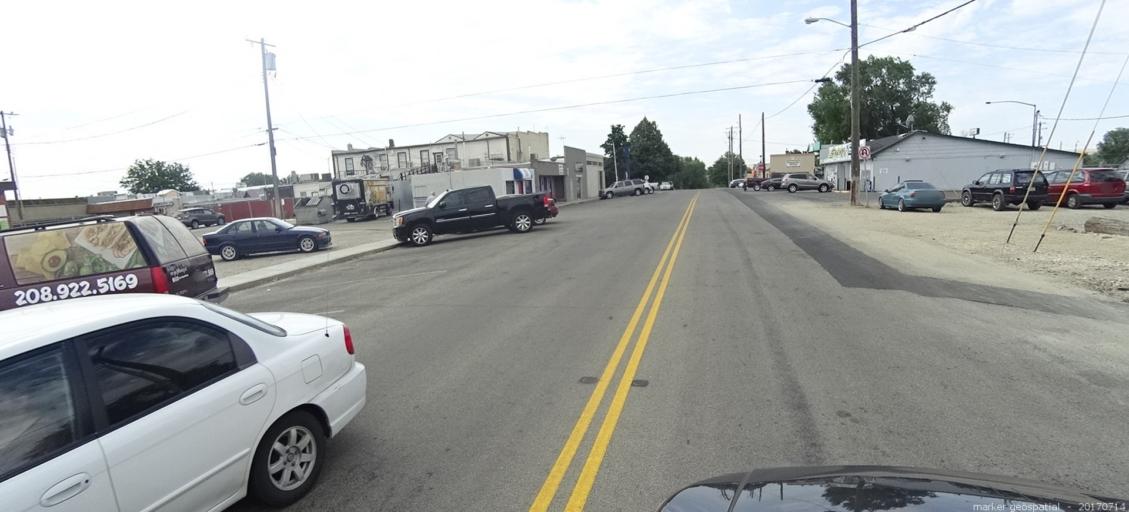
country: US
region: Idaho
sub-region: Ada County
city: Kuna
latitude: 43.4915
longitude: -116.4194
